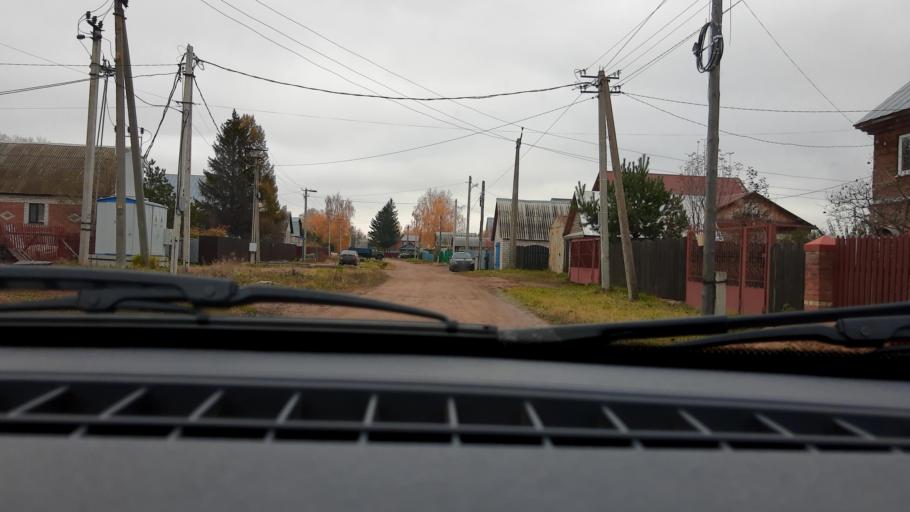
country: RU
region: Bashkortostan
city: Mikhaylovka
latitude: 54.7809
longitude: 55.8274
